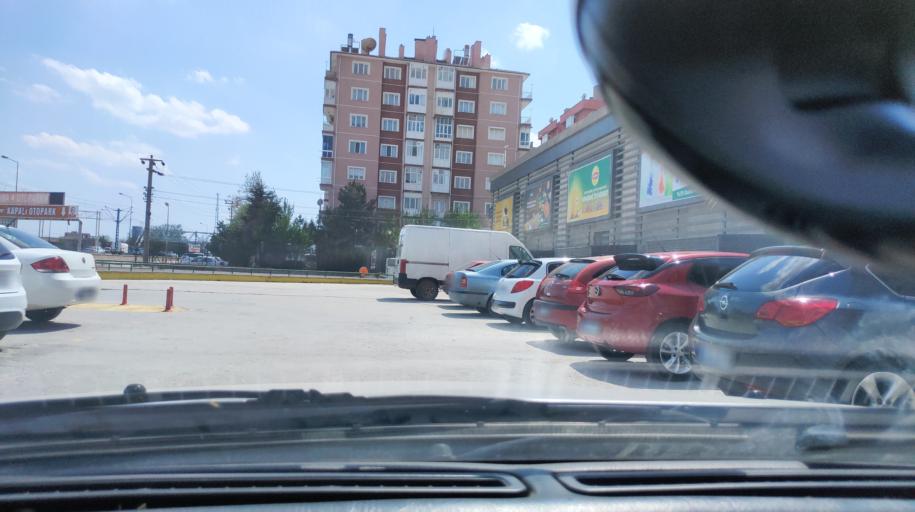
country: TR
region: Konya
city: Selcuklu
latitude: 37.9277
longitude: 32.5083
